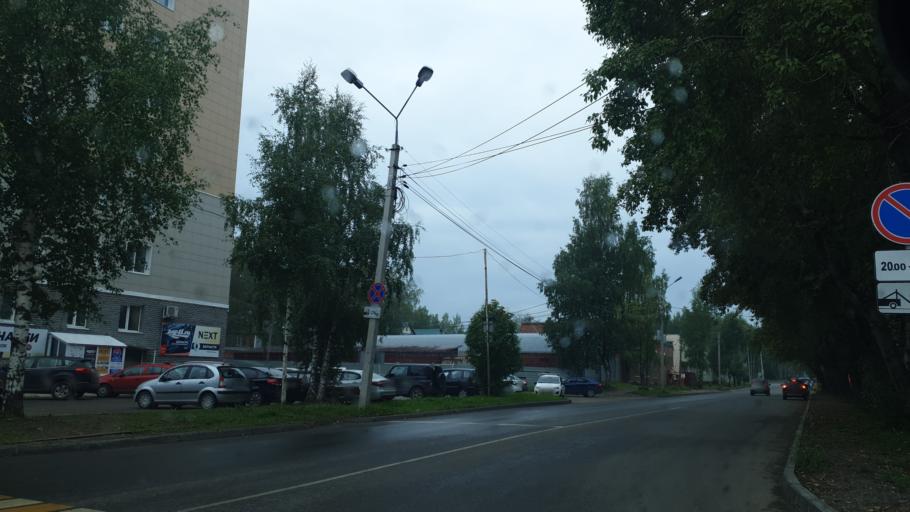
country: RU
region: Komi Republic
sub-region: Syktyvdinskiy Rayon
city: Syktyvkar
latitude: 61.6555
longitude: 50.8308
